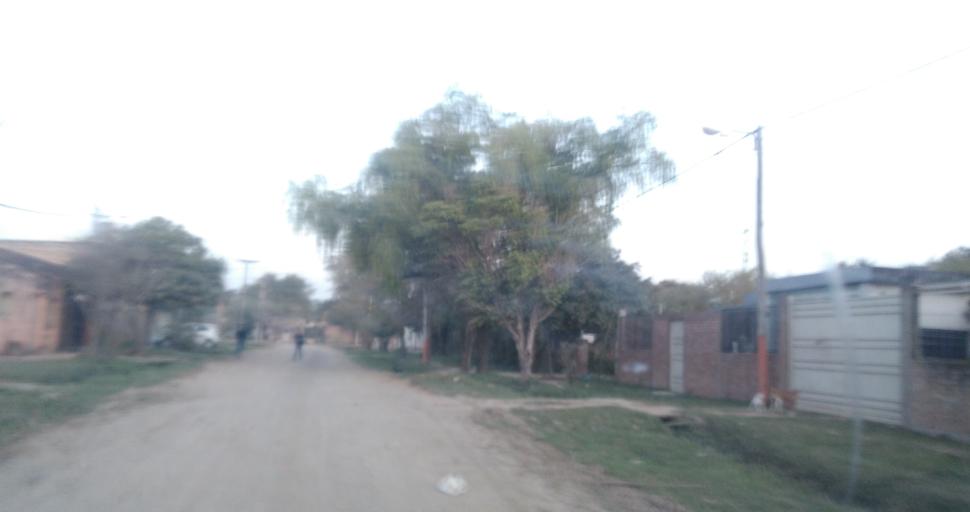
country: AR
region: Chaco
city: Resistencia
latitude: -27.4727
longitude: -59.0122
